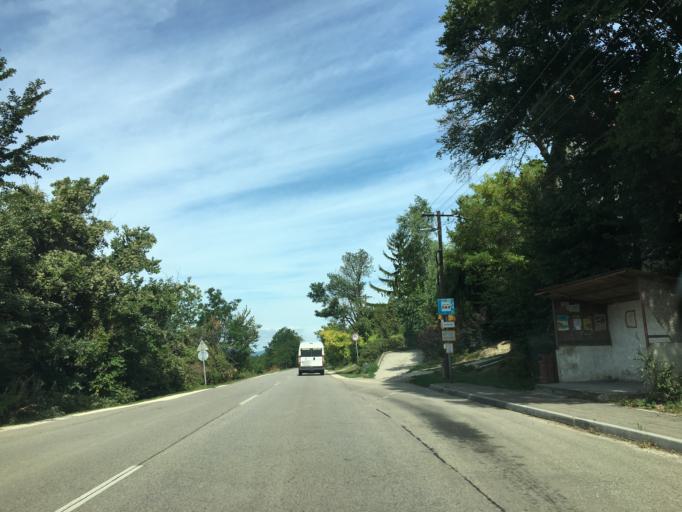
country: HU
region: Pest
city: Zsambek
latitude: 47.5684
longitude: 18.6864
